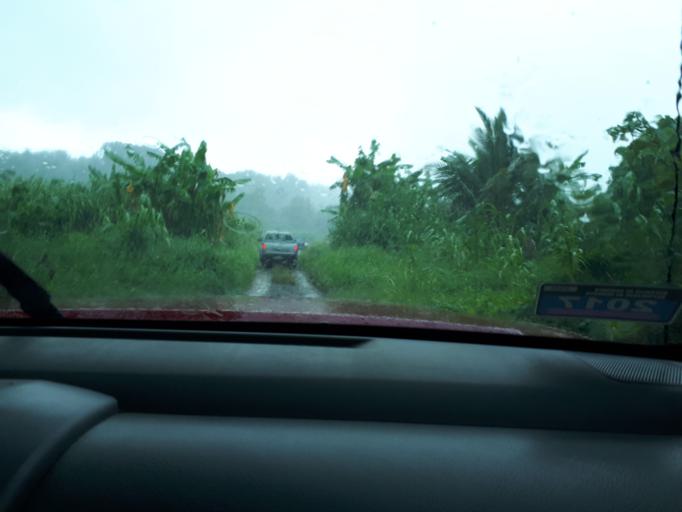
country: VU
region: Sanma
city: Luganville
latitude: -15.6108
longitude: 166.8700
